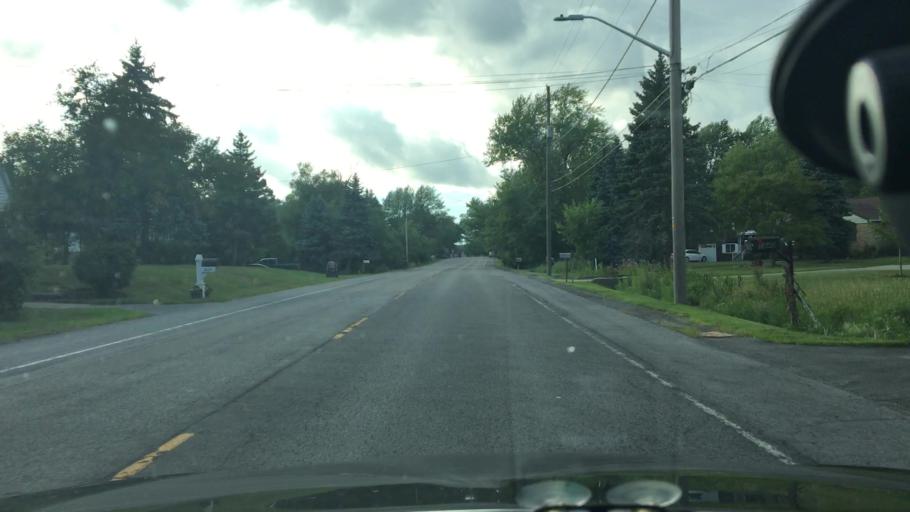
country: US
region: New York
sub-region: Erie County
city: Depew
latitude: 42.8367
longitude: -78.7154
